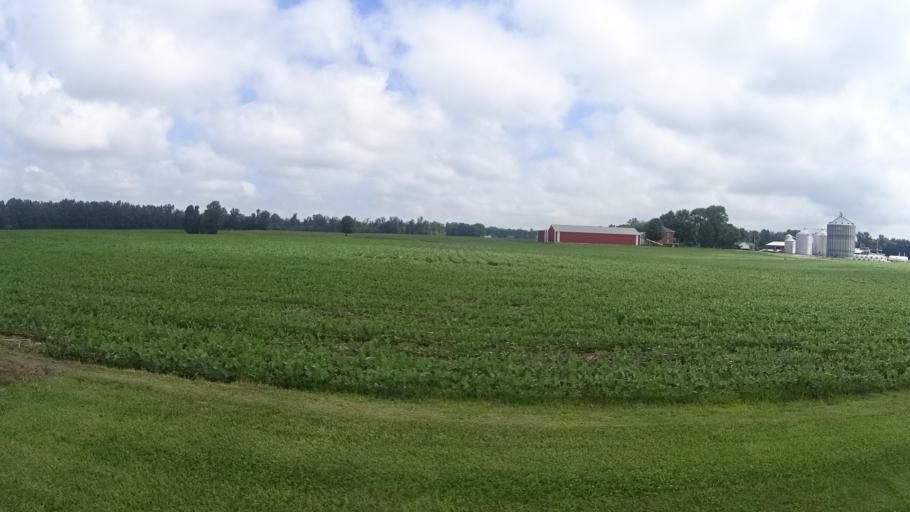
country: US
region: Ohio
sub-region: Huron County
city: Wakeman
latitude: 41.3058
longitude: -82.3884
